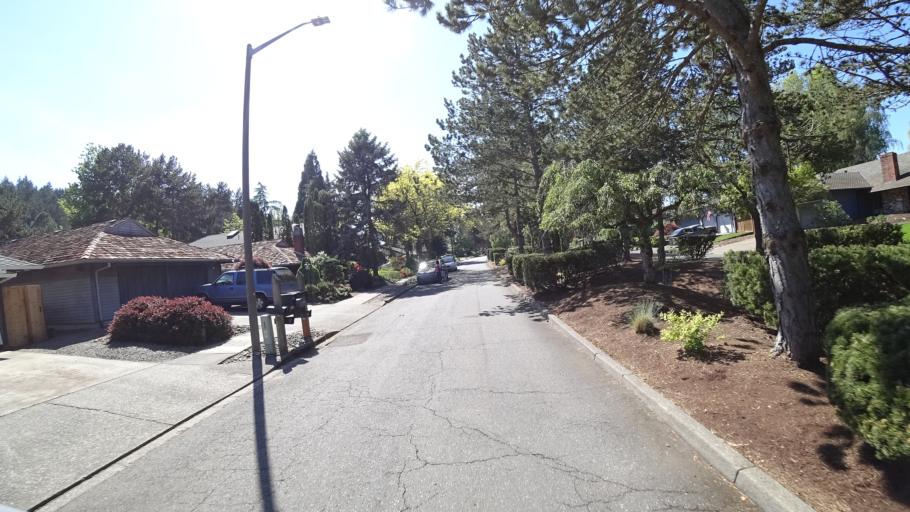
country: US
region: Oregon
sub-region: Washington County
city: Aloha
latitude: 45.4770
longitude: -122.8380
